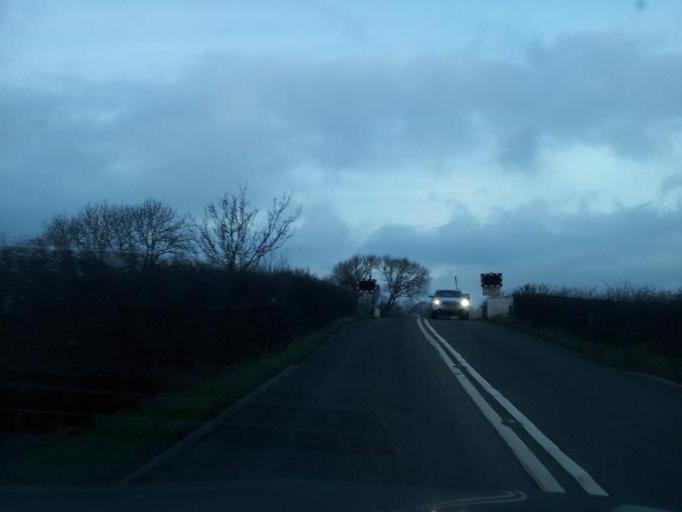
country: GB
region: England
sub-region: Derbyshire
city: Repton
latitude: 52.8569
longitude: -1.5645
